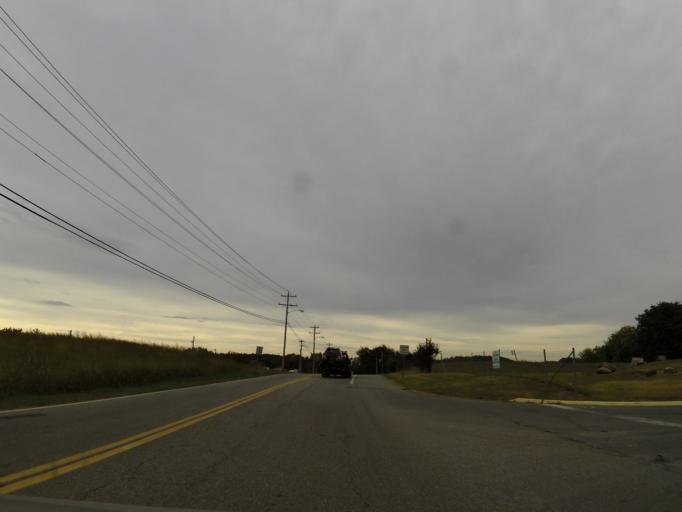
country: US
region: Tennessee
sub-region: Blount County
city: Alcoa
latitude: 35.8133
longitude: -83.9774
